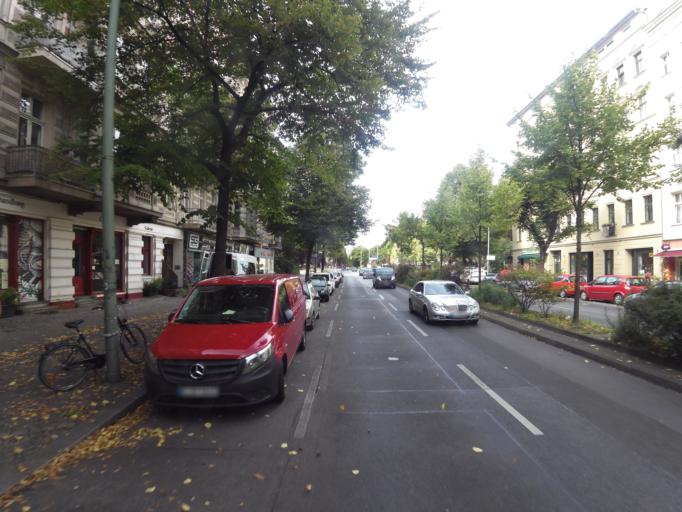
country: DE
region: Berlin
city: Bezirk Kreuzberg
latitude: 52.4915
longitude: 13.4141
